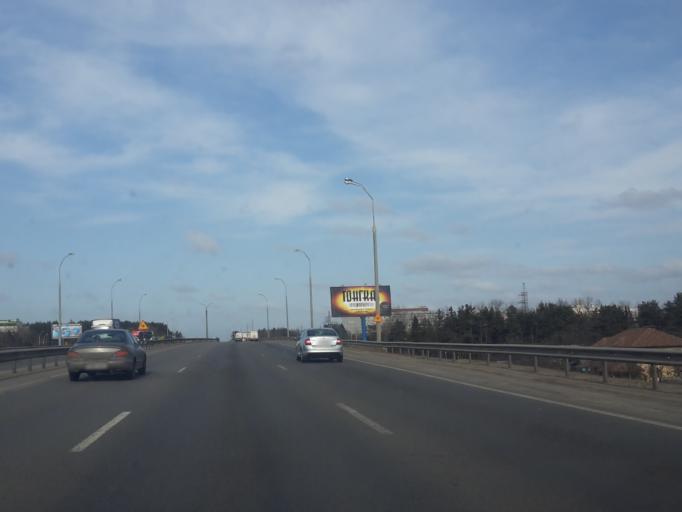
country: BY
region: Minsk
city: Vyaliki Trastsyanets
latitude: 53.9195
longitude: 27.6823
